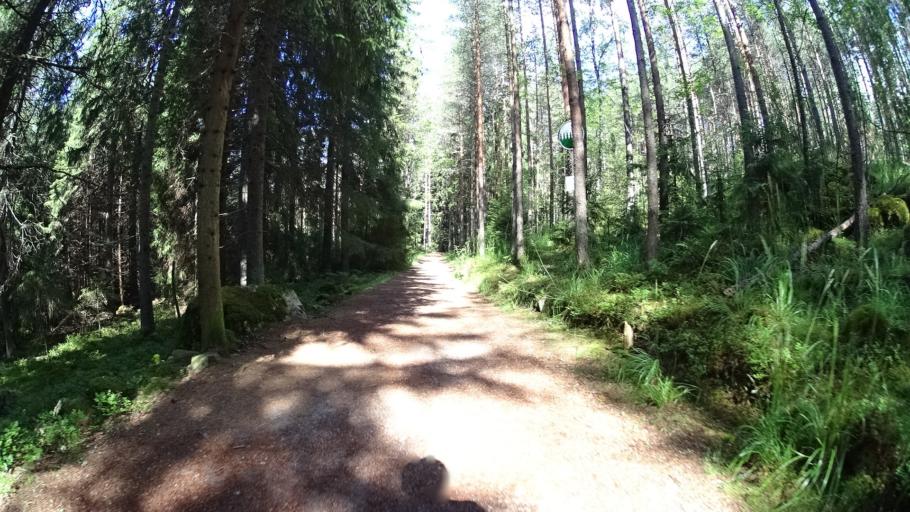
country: FI
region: Uusimaa
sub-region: Helsinki
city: Kauniainen
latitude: 60.3220
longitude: 24.6953
